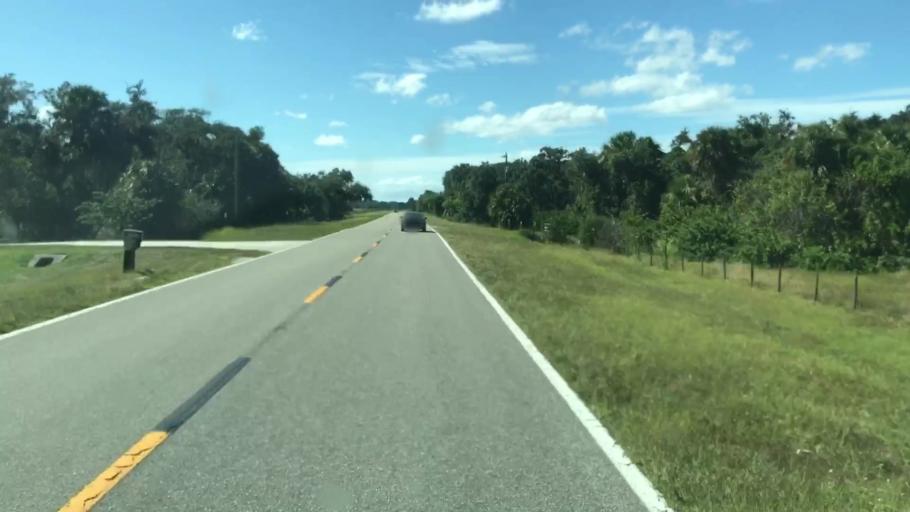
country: US
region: Florida
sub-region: Lee County
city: Olga
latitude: 26.7401
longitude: -81.7363
